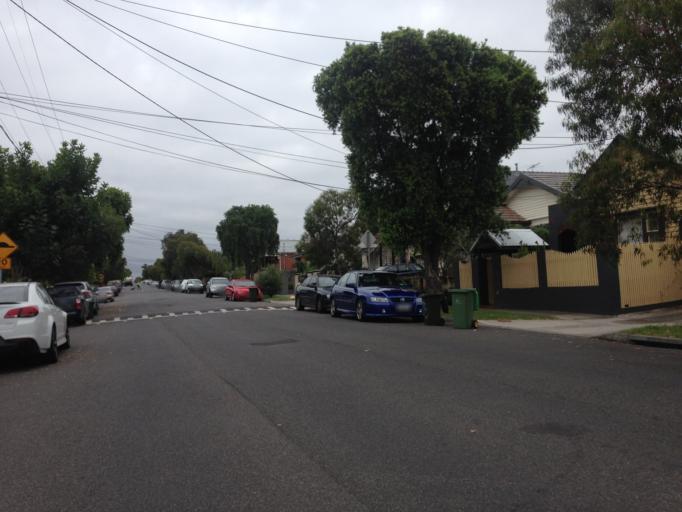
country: AU
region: Victoria
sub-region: Darebin
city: Thornbury
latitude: -37.7577
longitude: 145.0131
